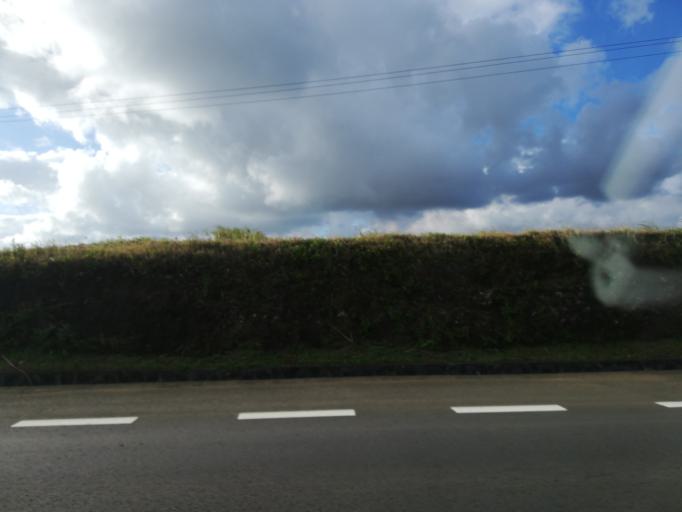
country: MU
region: Moka
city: Quartier Militaire
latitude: -20.2553
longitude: 57.5811
